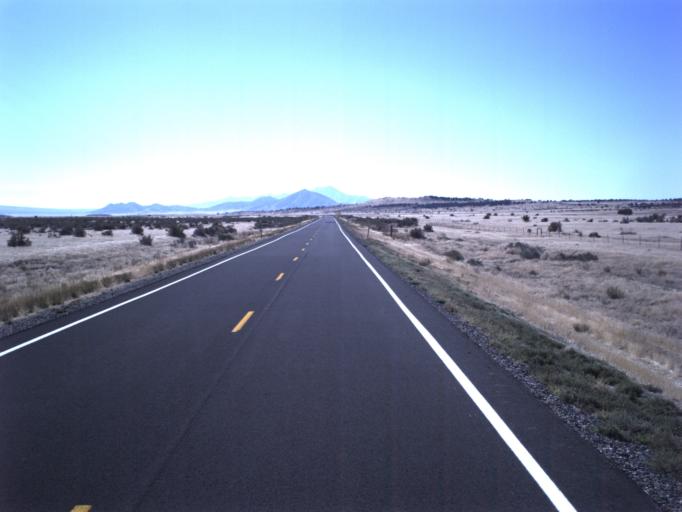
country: US
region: Utah
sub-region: Tooele County
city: Grantsville
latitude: 40.2668
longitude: -112.7412
